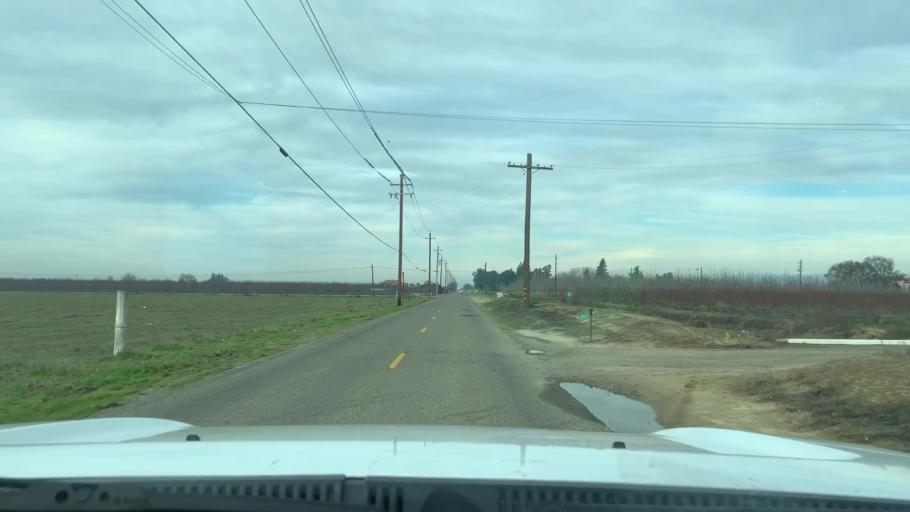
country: US
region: California
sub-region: Fresno County
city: Selma
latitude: 36.5742
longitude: -119.5750
